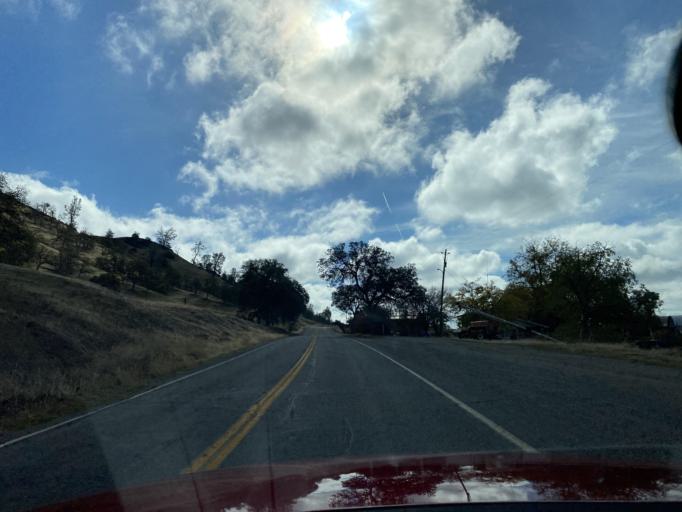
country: US
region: California
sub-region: Glenn County
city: Willows
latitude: 39.5579
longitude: -122.5422
